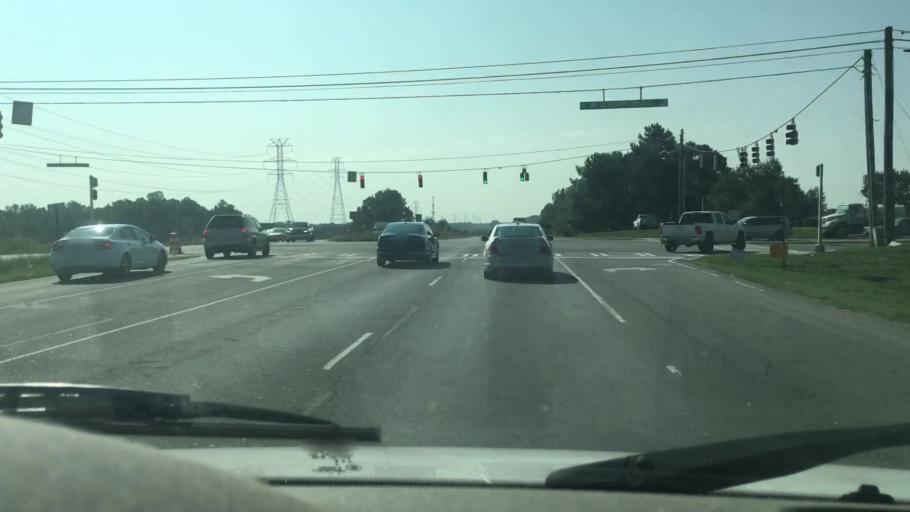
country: US
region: North Carolina
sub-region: Gaston County
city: Mount Holly
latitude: 35.3259
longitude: -80.9457
